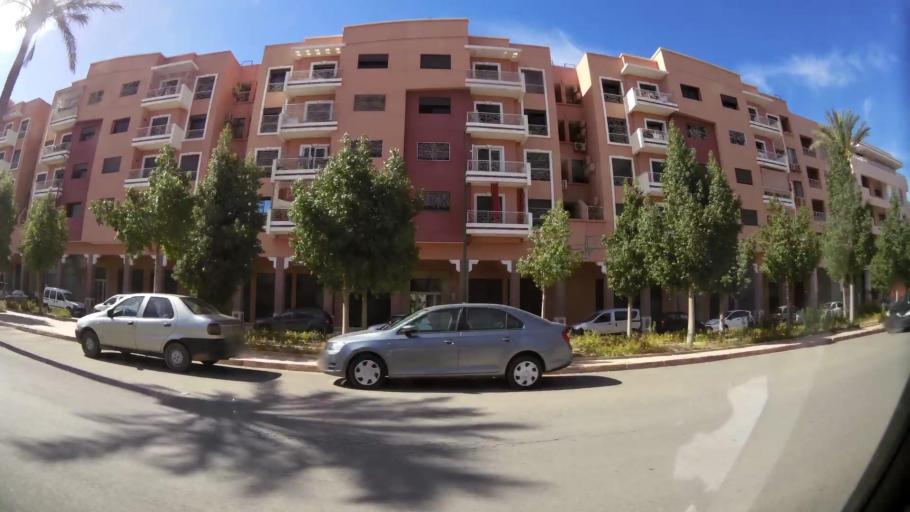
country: MA
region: Marrakech-Tensift-Al Haouz
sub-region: Marrakech
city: Marrakesh
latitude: 31.6648
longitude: -8.0259
